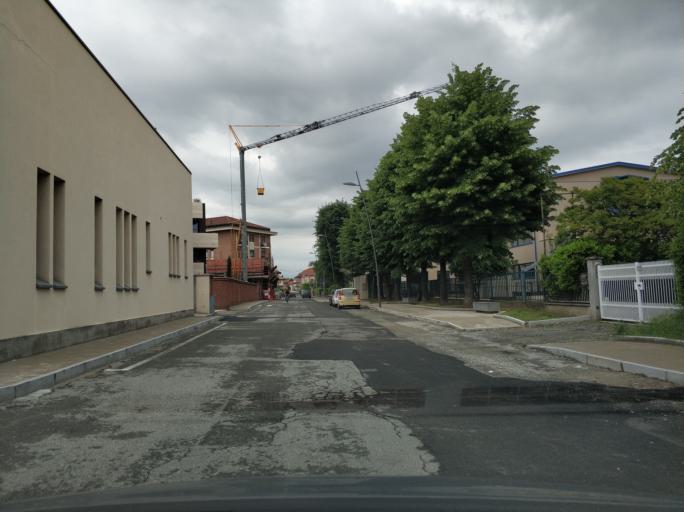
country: IT
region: Piedmont
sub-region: Provincia di Torino
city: Cirie
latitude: 45.2283
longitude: 7.6076
